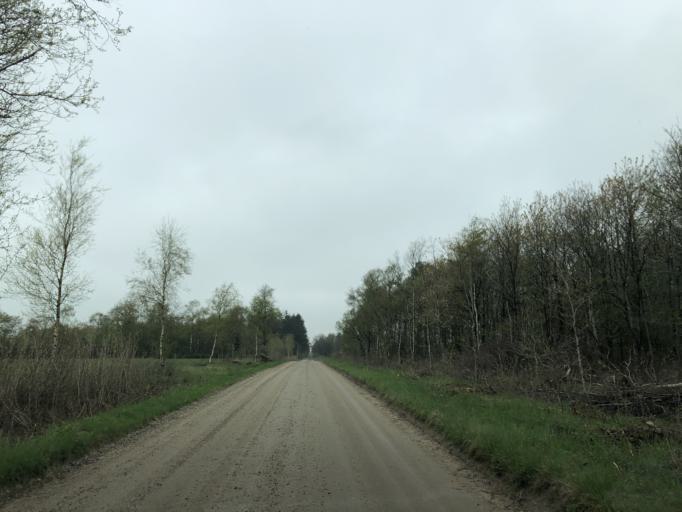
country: DK
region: Central Jutland
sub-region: Lemvig Kommune
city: Lemvig
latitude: 56.5034
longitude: 8.3282
